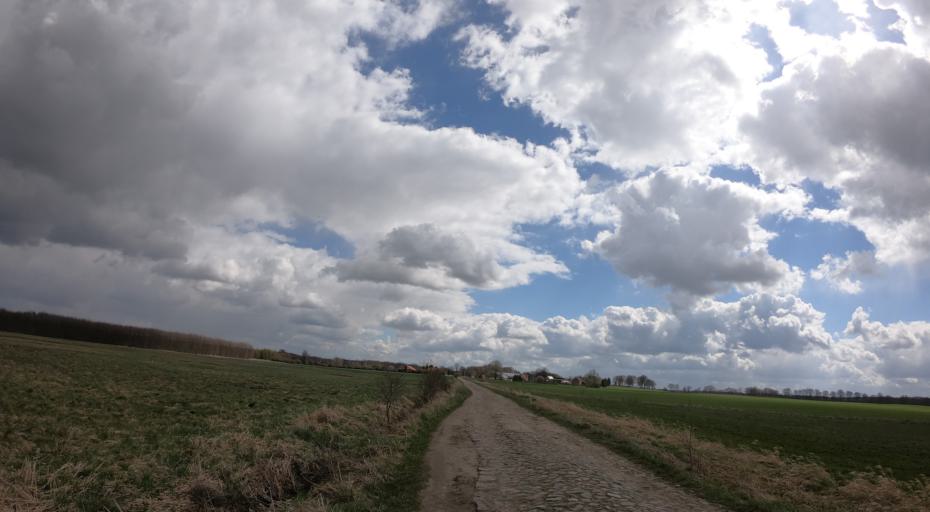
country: PL
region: West Pomeranian Voivodeship
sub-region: Powiat drawski
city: Drawsko Pomorskie
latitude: 53.5443
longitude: 15.8650
